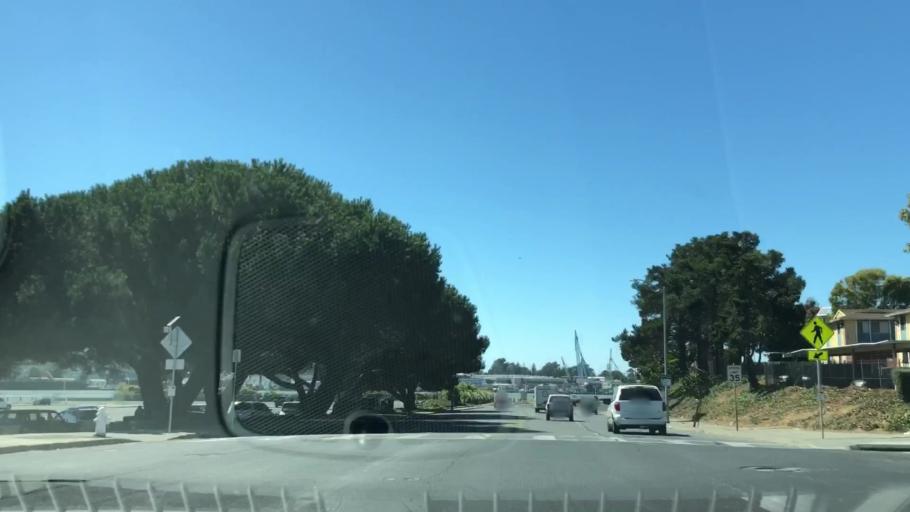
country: US
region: California
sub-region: Solano County
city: Vallejo
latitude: 38.0972
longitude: -122.2566
